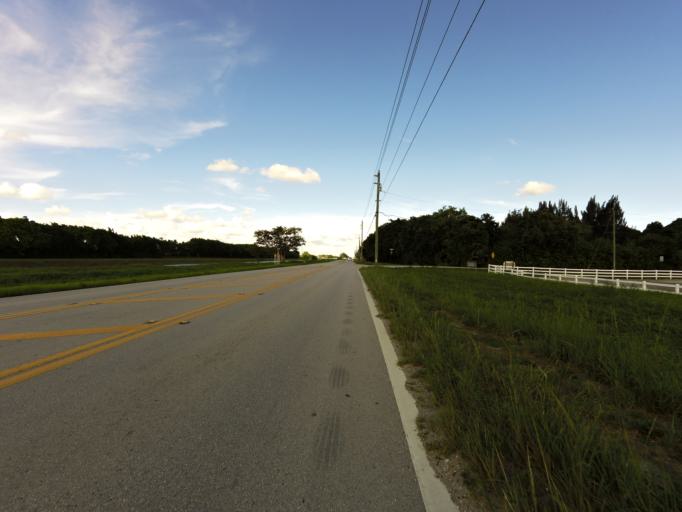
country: US
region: Florida
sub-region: Broward County
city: Weston
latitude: 26.0615
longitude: -80.4075
